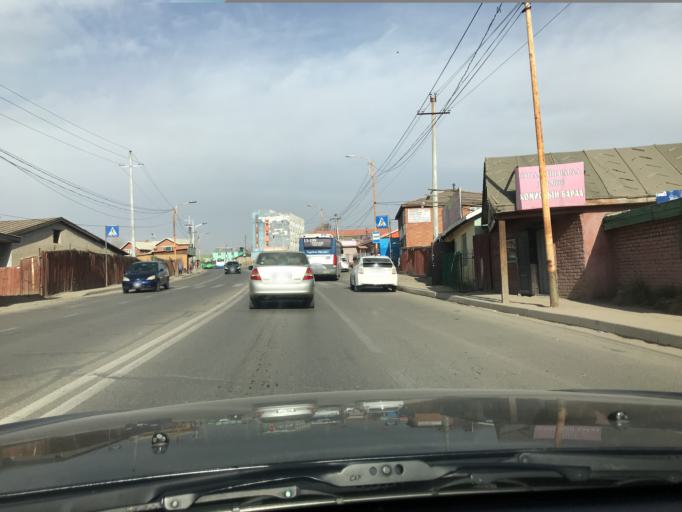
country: MN
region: Ulaanbaatar
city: Ulaanbaatar
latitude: 47.9328
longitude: 106.8873
